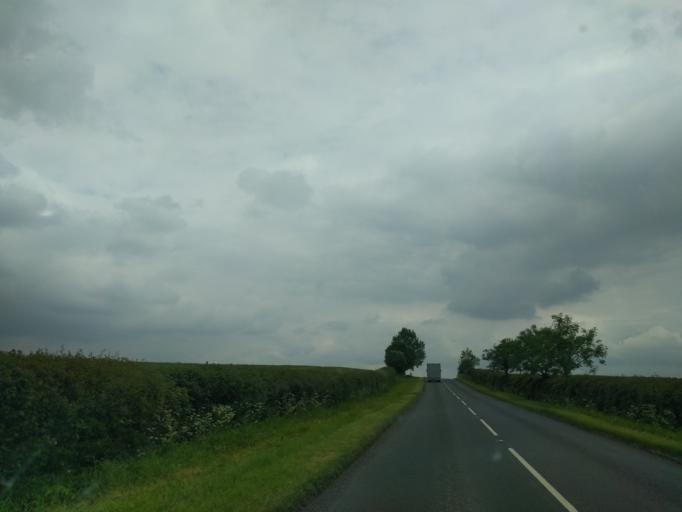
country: GB
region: England
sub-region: Somerset
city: Ilchester
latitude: 51.0757
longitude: -2.6623
